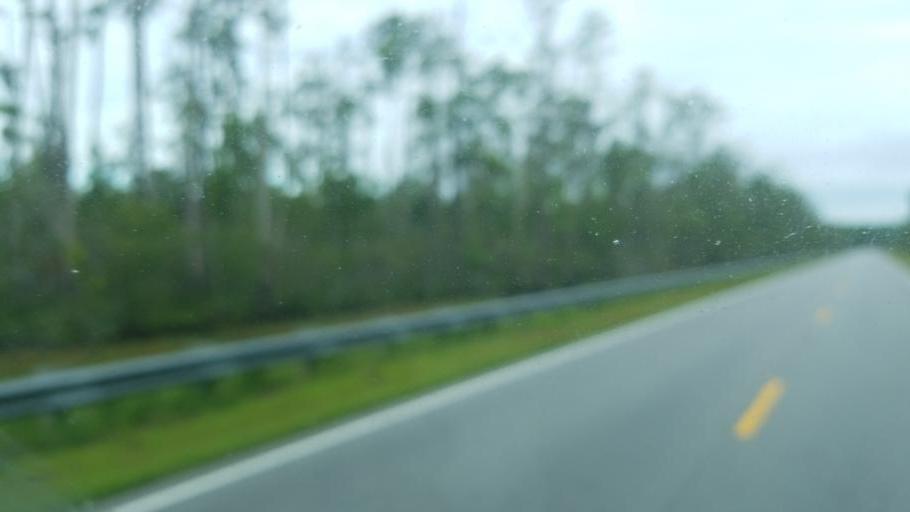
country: US
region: North Carolina
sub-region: Tyrrell County
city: Columbia
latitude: 35.9005
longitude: -76.0648
